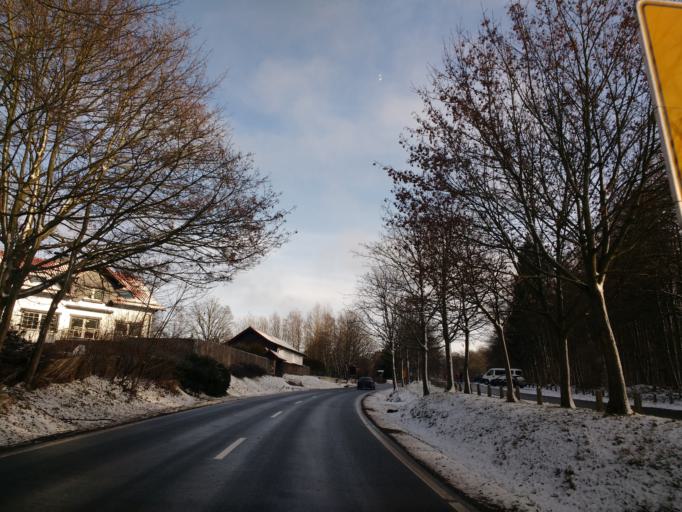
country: DE
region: Saxony-Anhalt
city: Friedrichsbrunn
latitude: 51.6942
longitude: 11.0476
